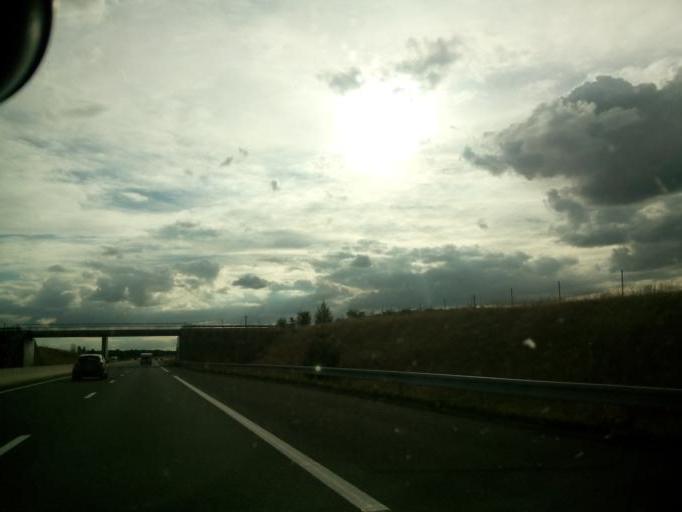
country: FR
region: Centre
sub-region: Departement du Loir-et-Cher
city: Faverolles-sur-Cher
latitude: 47.2977
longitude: 1.1936
